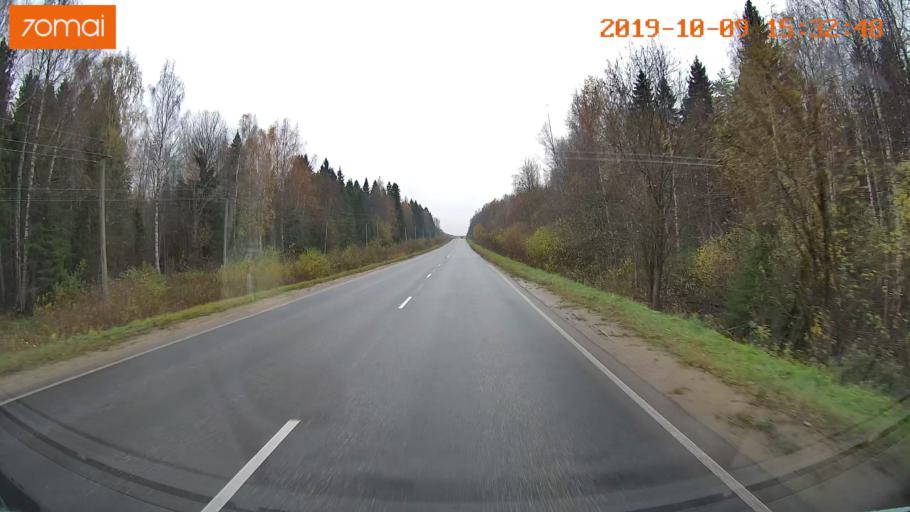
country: RU
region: Kostroma
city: Oktyabr'skiy
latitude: 57.9603
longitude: 41.2709
